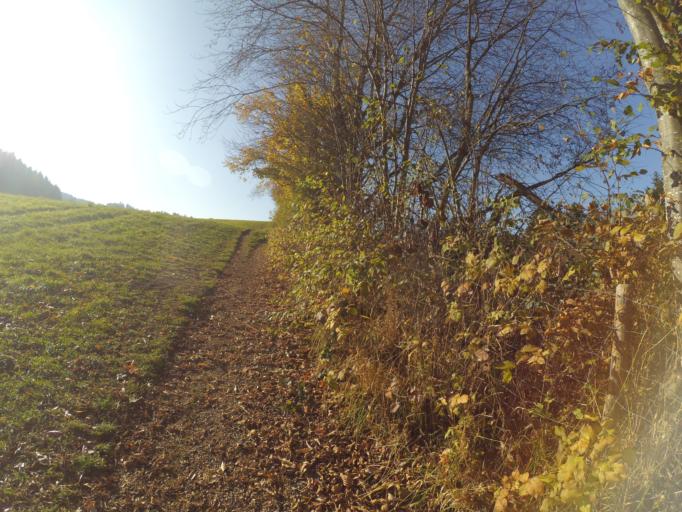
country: DE
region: Bavaria
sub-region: Upper Bavaria
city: Bernbeuren
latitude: 47.7379
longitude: 10.7656
